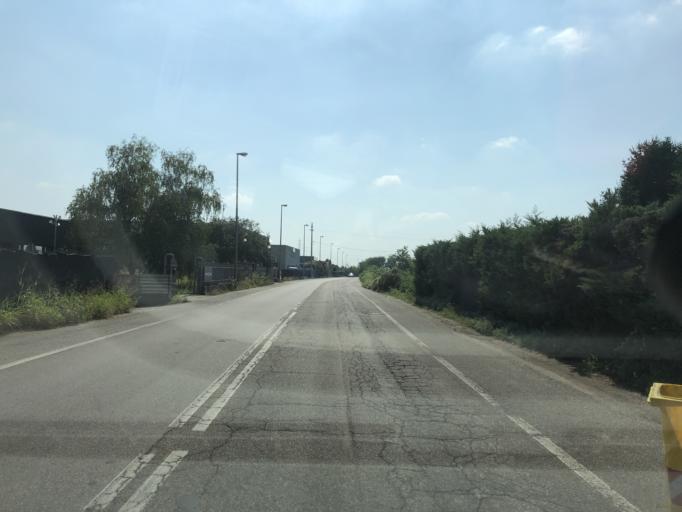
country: IT
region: Veneto
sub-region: Provincia di Verona
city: Bassone
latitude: 45.4458
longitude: 10.8983
